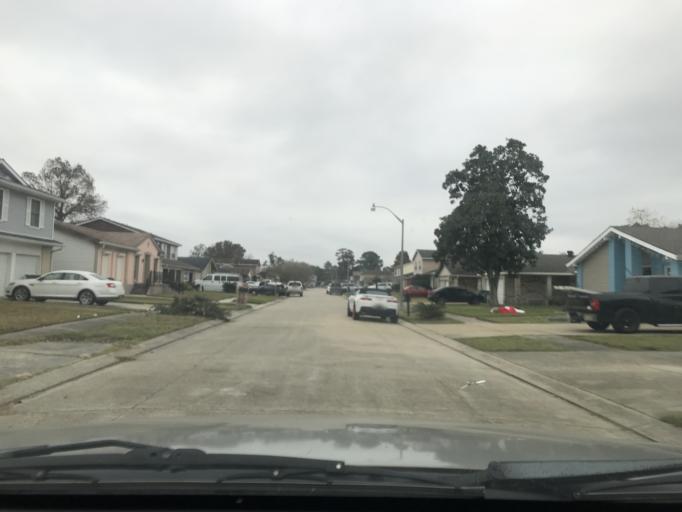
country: US
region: Louisiana
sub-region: Jefferson Parish
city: Woodmere
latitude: 29.8665
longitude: -90.0785
